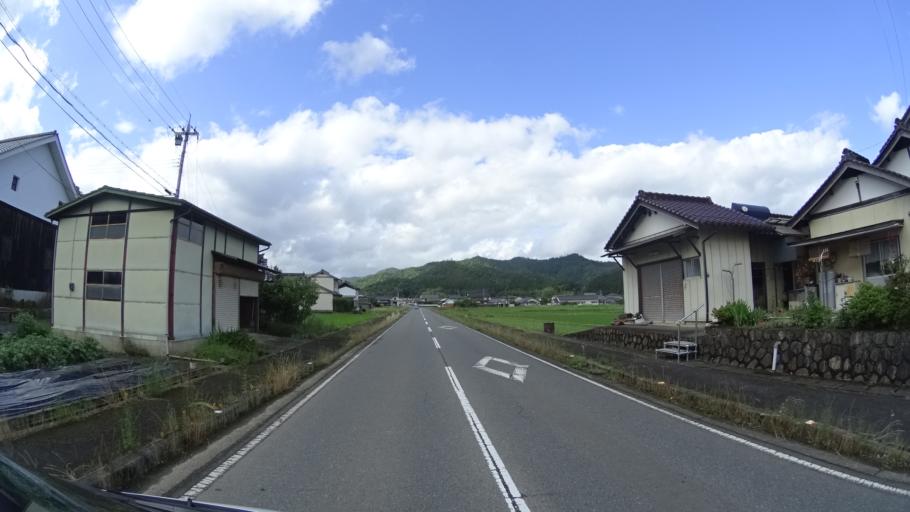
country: JP
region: Kyoto
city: Ayabe
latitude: 35.3652
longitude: 135.2388
